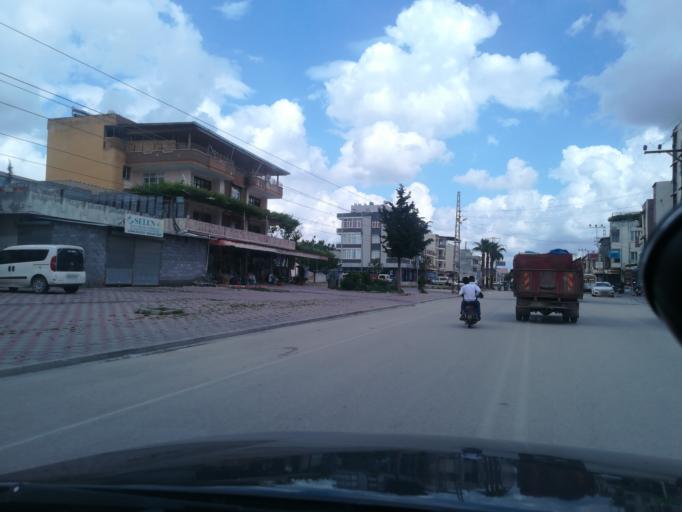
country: TR
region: Adana
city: Yuregir
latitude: 36.9773
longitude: 35.3837
